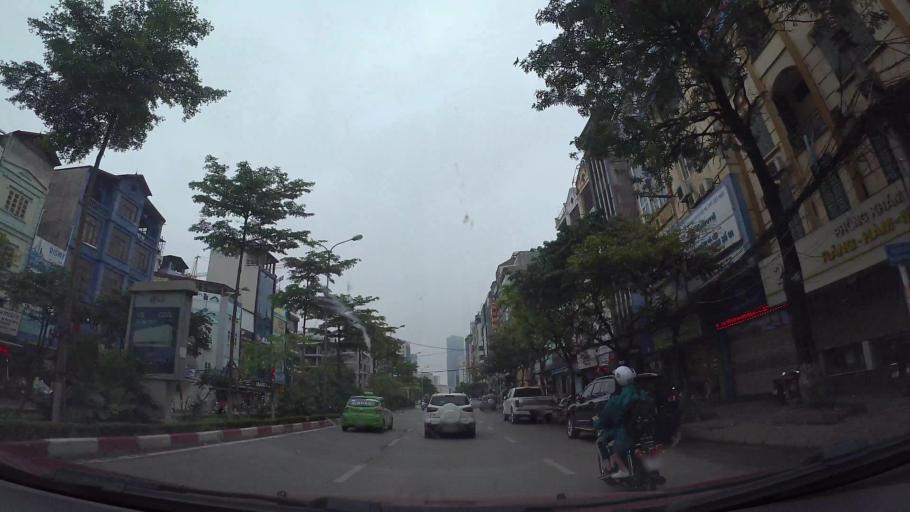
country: VN
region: Ha Noi
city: Cau Giay
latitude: 21.0354
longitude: 105.7891
